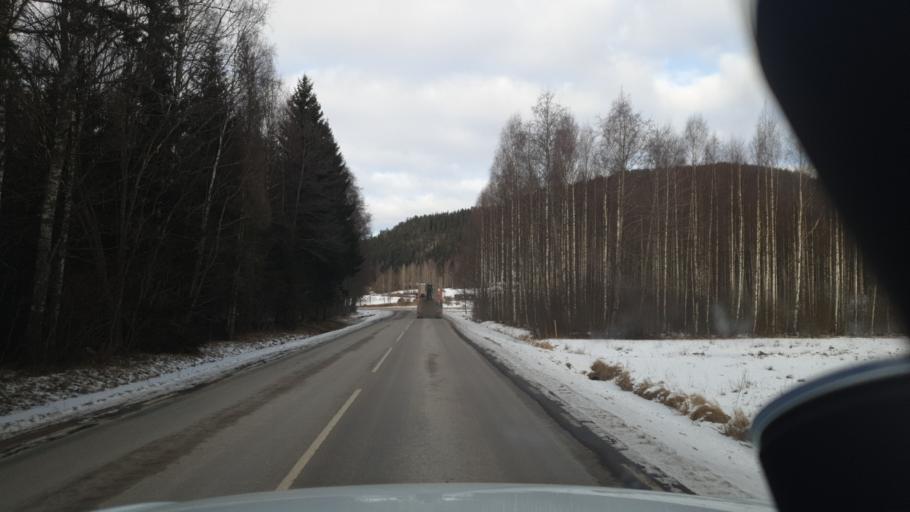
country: SE
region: Vaermland
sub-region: Arvika Kommun
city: Arvika
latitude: 59.7464
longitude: 12.6389
